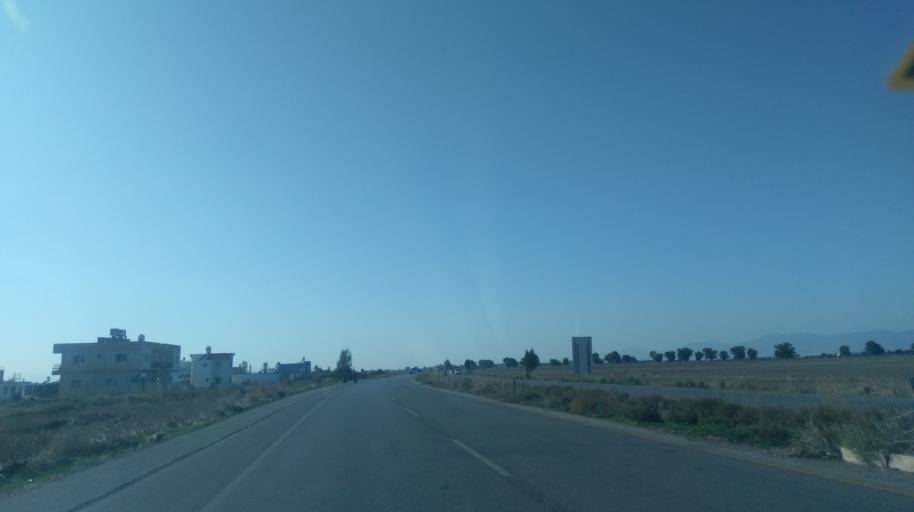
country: CY
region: Ammochostos
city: Lefkonoiko
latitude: 35.1711
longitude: 33.7851
